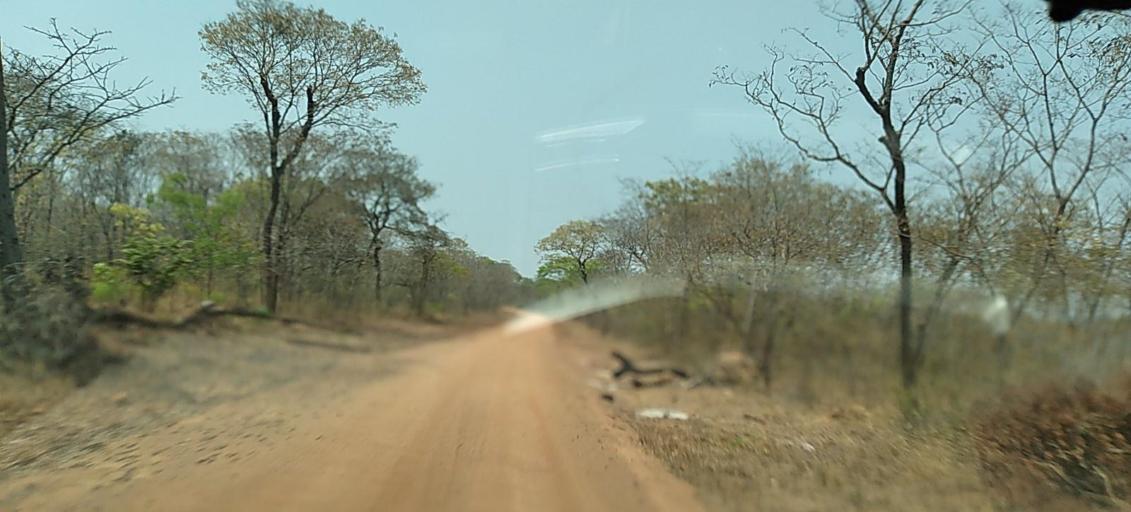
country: ZM
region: Central
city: Mumbwa
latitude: -14.2777
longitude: 26.5254
